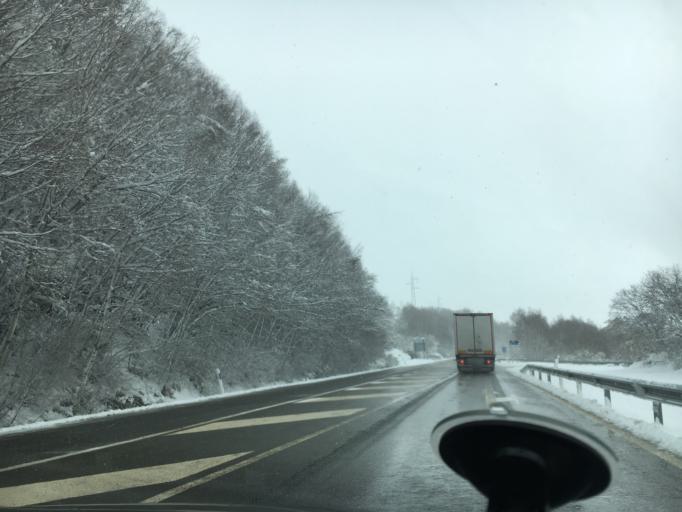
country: ES
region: Castille and Leon
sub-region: Provincia de Zamora
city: Lubian
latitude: 42.0355
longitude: -6.8457
